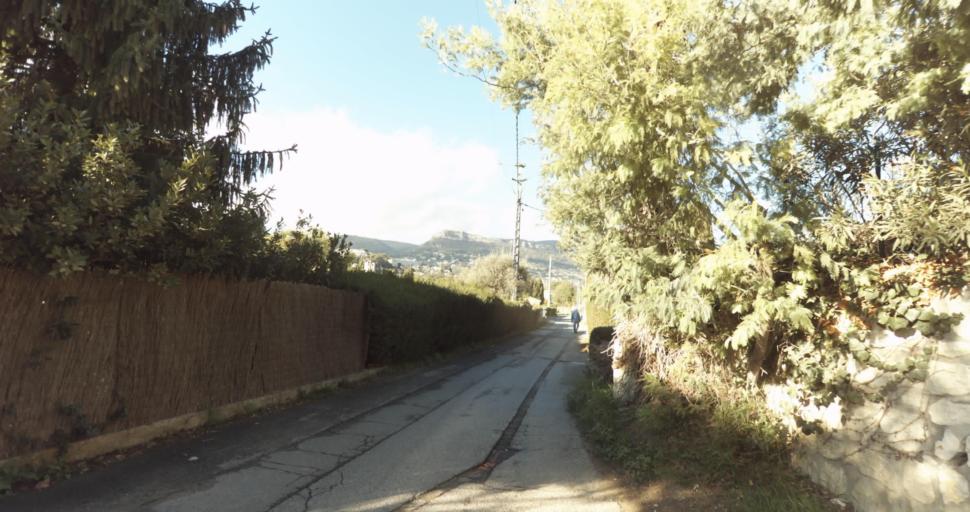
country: FR
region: Provence-Alpes-Cote d'Azur
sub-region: Departement des Alpes-Maritimes
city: Saint-Paul-de-Vence
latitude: 43.7116
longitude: 7.1321
